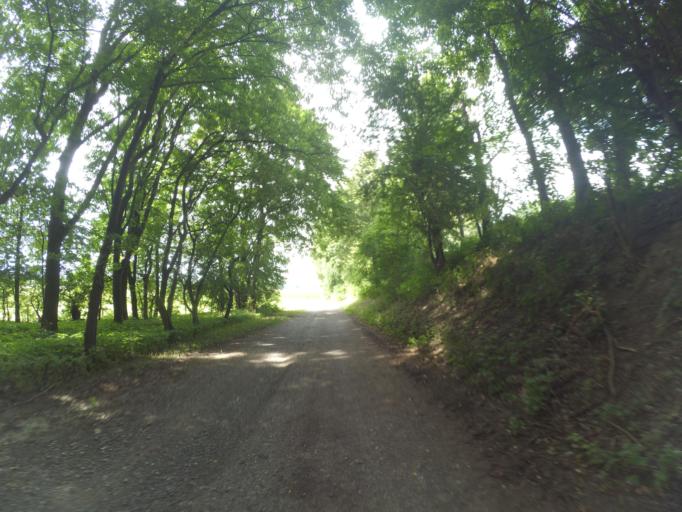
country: DE
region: Bavaria
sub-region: Swabia
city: Jengen
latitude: 48.0169
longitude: 10.7298
